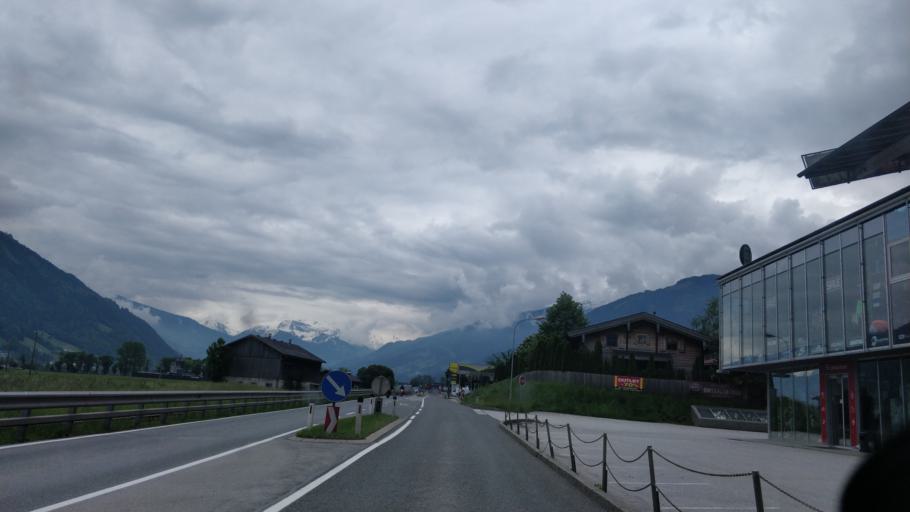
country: AT
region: Tyrol
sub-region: Politischer Bezirk Schwaz
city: Fugen
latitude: 47.3526
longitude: 11.8514
